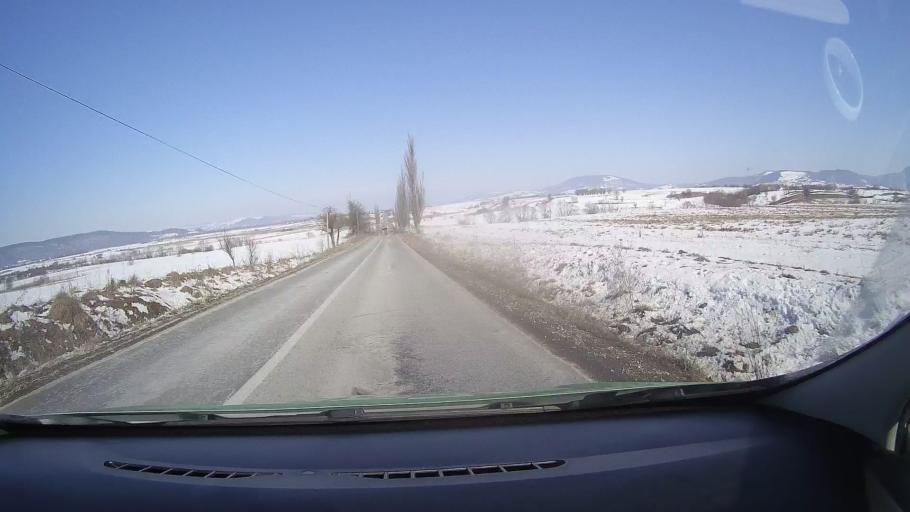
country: RO
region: Brasov
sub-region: Comuna Parau
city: Parau
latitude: 45.8587
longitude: 25.1974
